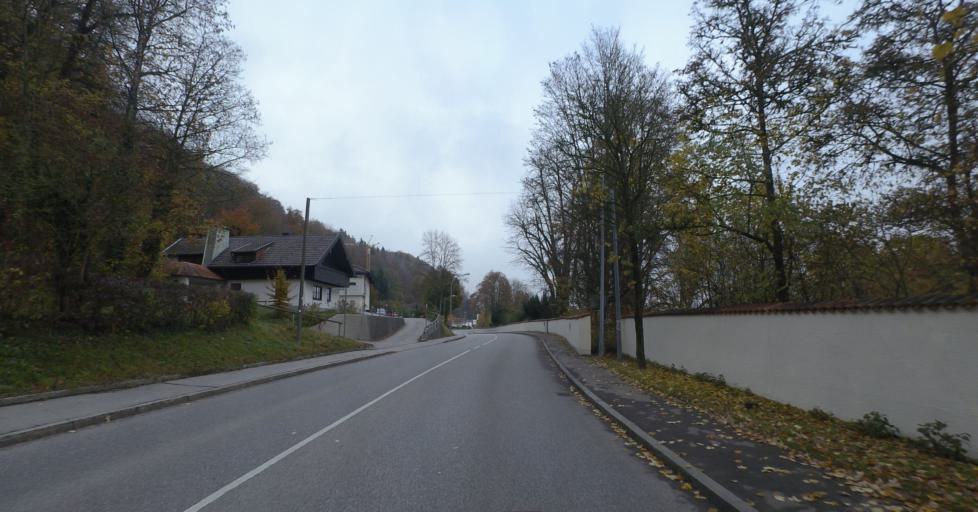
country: DE
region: Bavaria
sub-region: Upper Bavaria
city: Trostberg an der Alz
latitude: 48.0317
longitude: 12.5572
